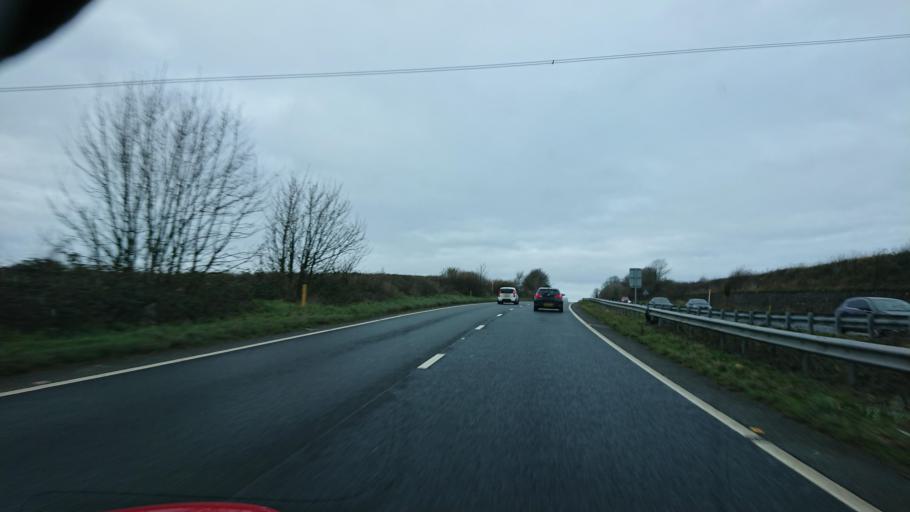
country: GB
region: England
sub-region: Cornwall
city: Liskeard
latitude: 50.4363
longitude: -4.4421
